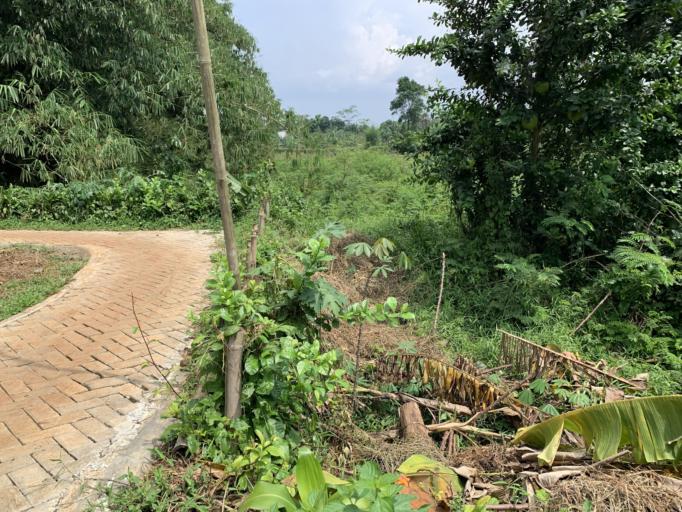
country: ID
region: West Java
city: Serpong
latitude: -6.4004
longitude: 106.6244
